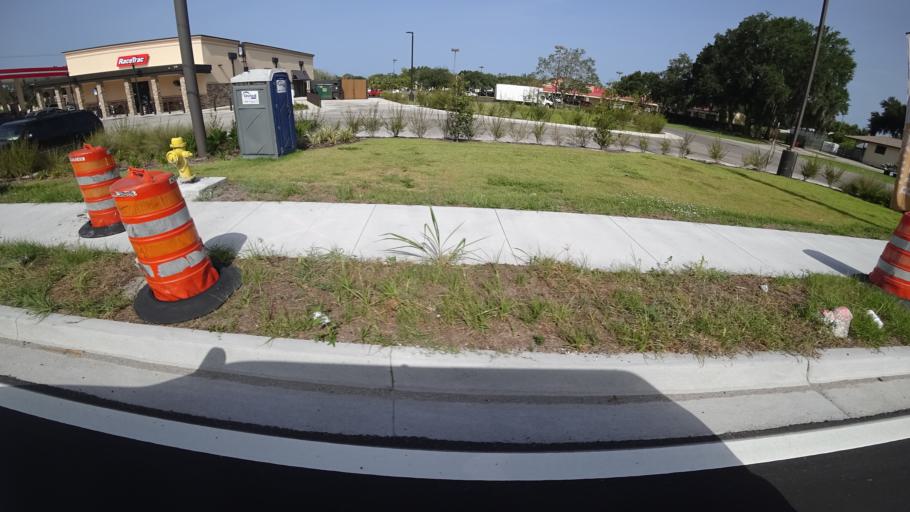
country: US
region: Florida
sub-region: Manatee County
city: Ellenton
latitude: 27.5227
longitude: -82.5284
